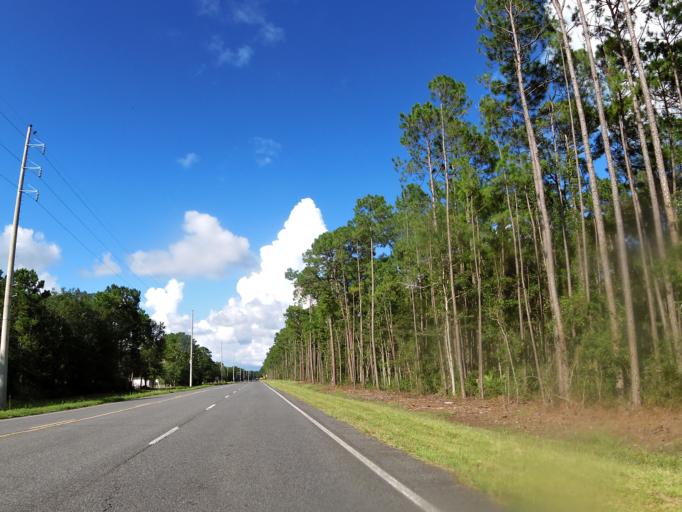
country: US
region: Georgia
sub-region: Glynn County
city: Brunswick
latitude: 31.1250
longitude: -81.6050
